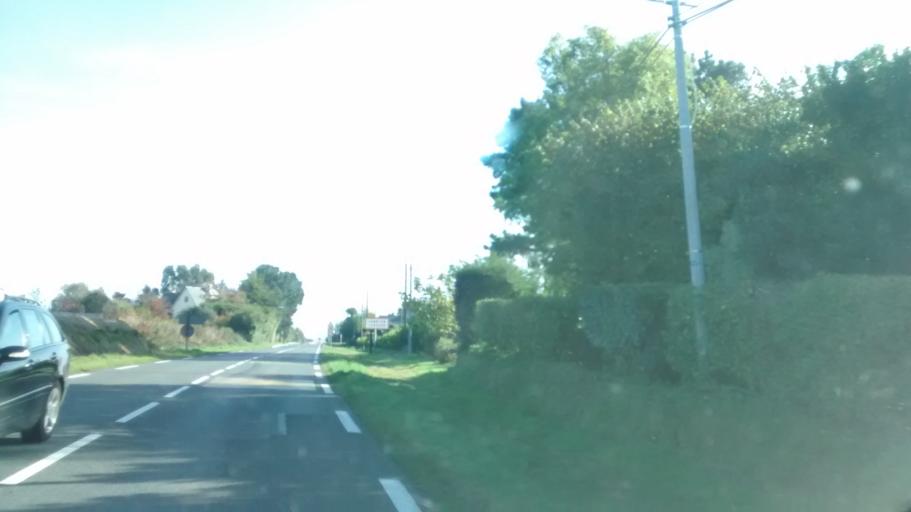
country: FR
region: Brittany
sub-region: Departement des Cotes-d'Armor
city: Pleumeur-Bodou
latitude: 48.7512
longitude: -3.4941
